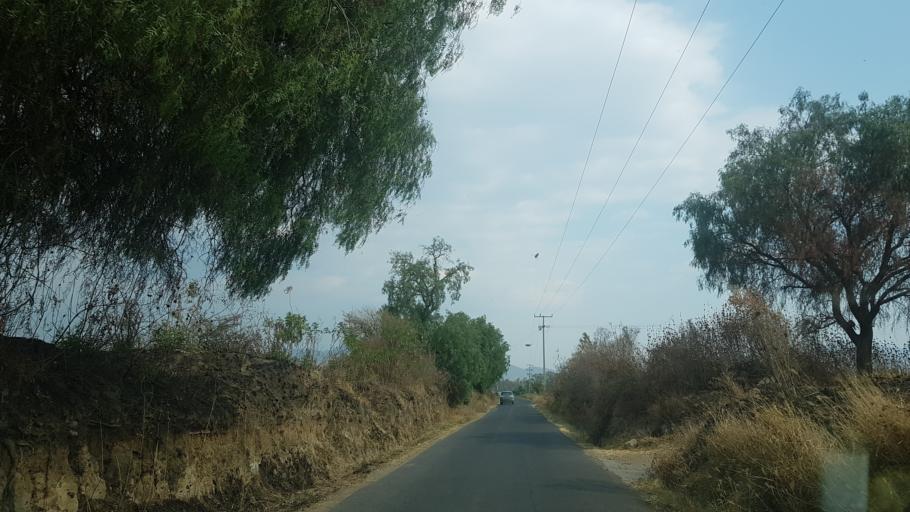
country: MX
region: Puebla
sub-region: Santa Isabel Cholula
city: Santa Ana Acozautla
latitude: 18.9526
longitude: -98.3984
